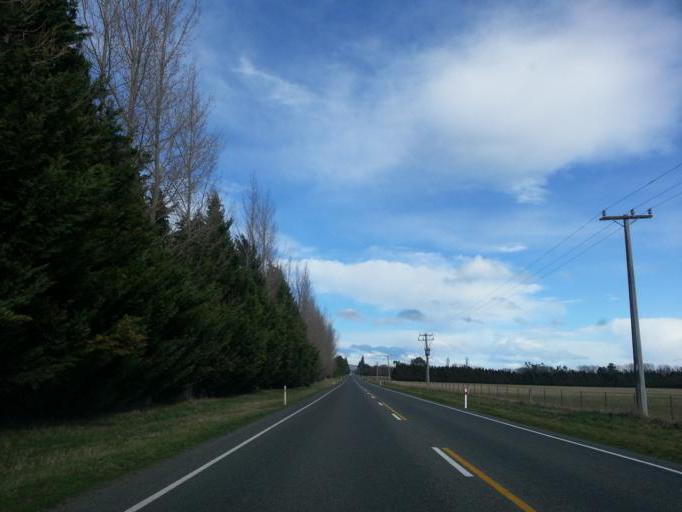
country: NZ
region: Canterbury
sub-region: Hurunui District
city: Amberley
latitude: -42.7827
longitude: 172.8412
